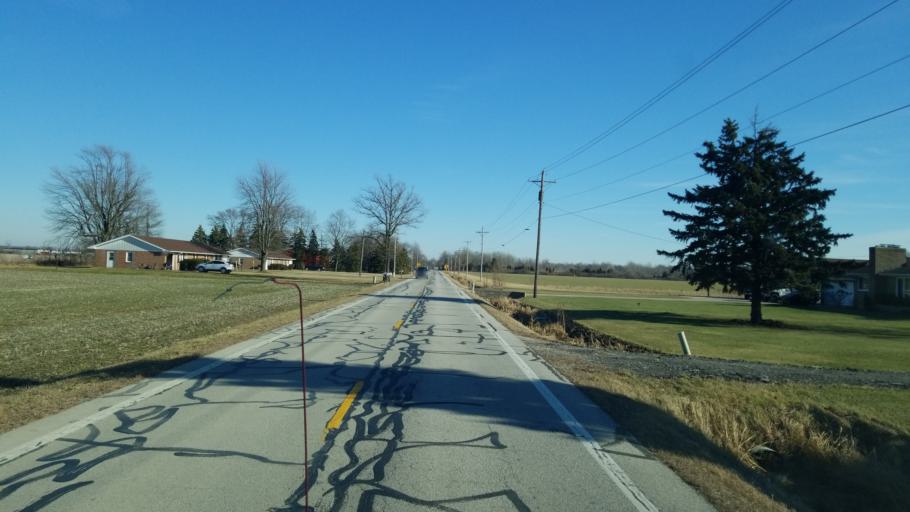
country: US
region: Ohio
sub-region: Wood County
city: Luckey
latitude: 41.4570
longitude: -83.4983
